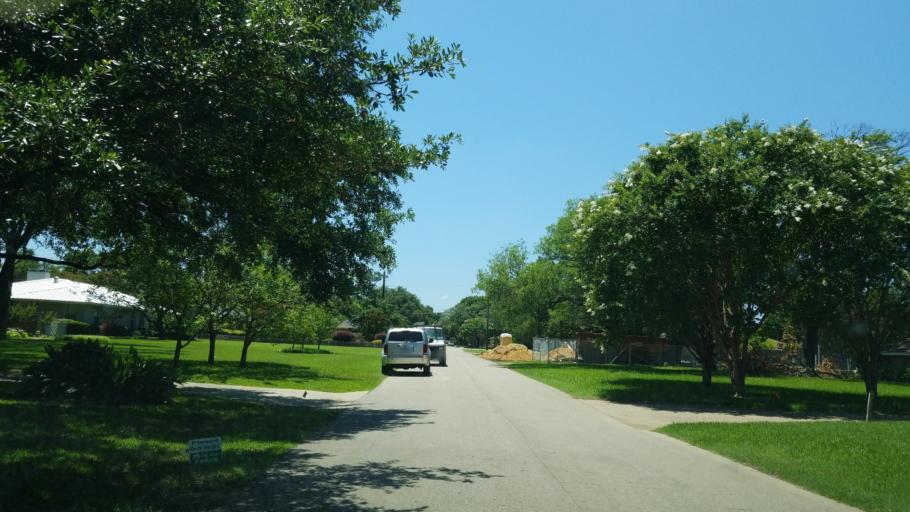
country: US
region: Texas
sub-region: Dallas County
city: University Park
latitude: 32.8779
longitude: -96.8370
